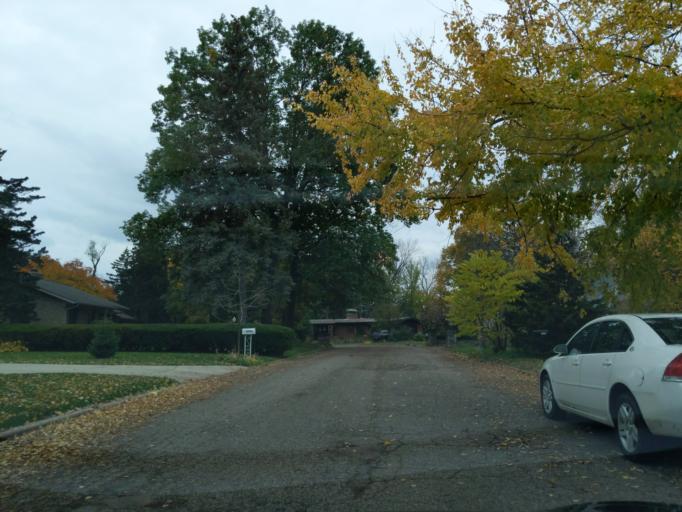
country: US
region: Michigan
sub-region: Ingham County
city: Edgemont Park
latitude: 42.7143
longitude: -84.5936
